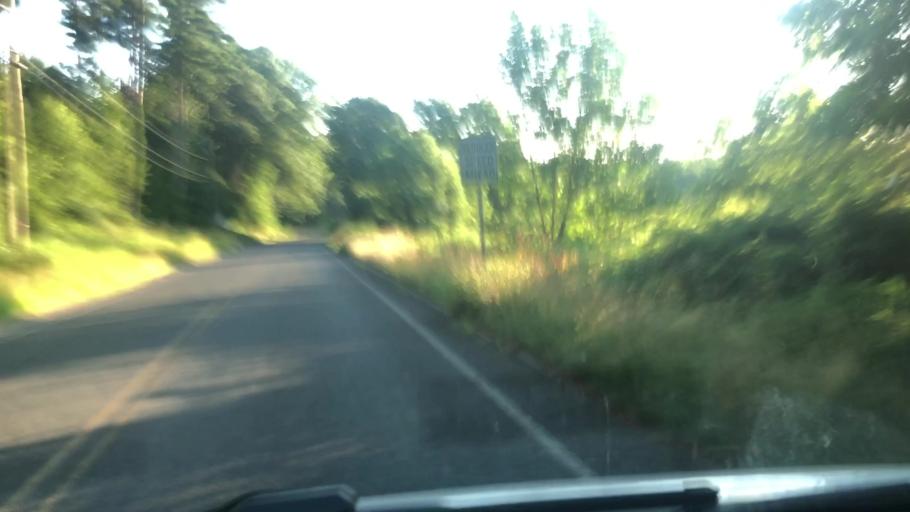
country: US
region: Massachusetts
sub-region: Hampshire County
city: Southampton
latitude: 42.2723
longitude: -72.7170
